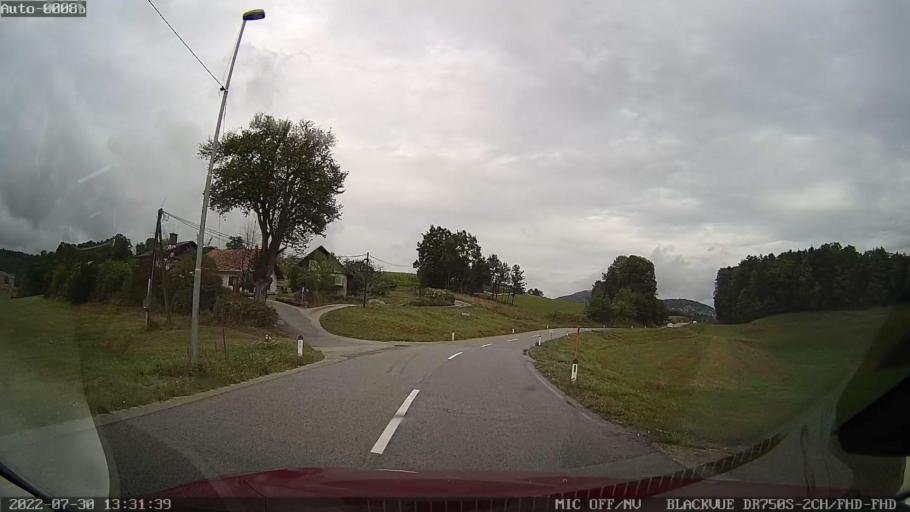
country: SI
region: Zuzemberk
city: Zuzemberk
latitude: 45.8383
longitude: 14.9366
